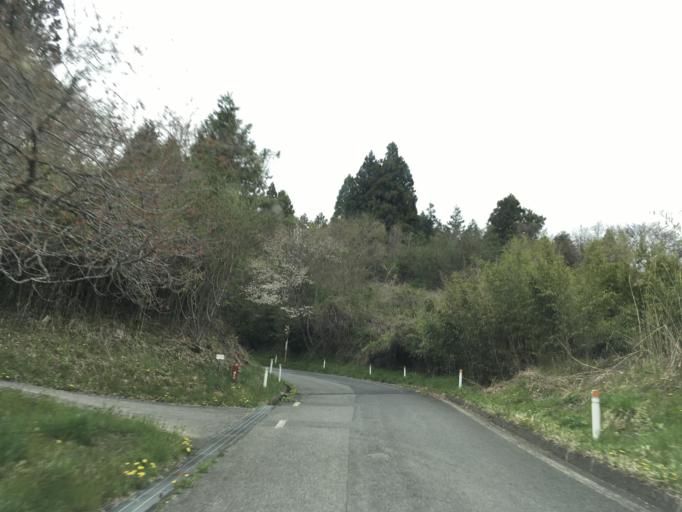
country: JP
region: Iwate
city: Ichinoseki
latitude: 38.8362
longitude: 141.3381
